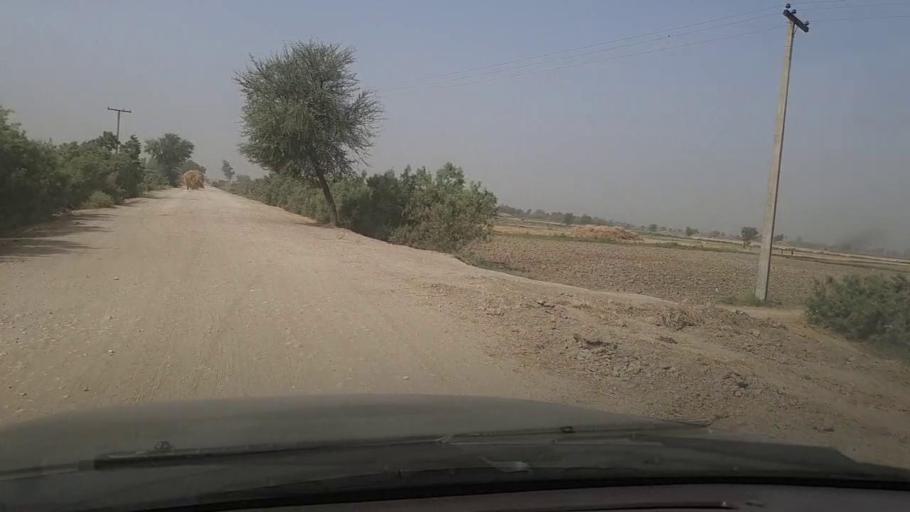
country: PK
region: Sindh
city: Shikarpur
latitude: 27.8990
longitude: 68.5895
